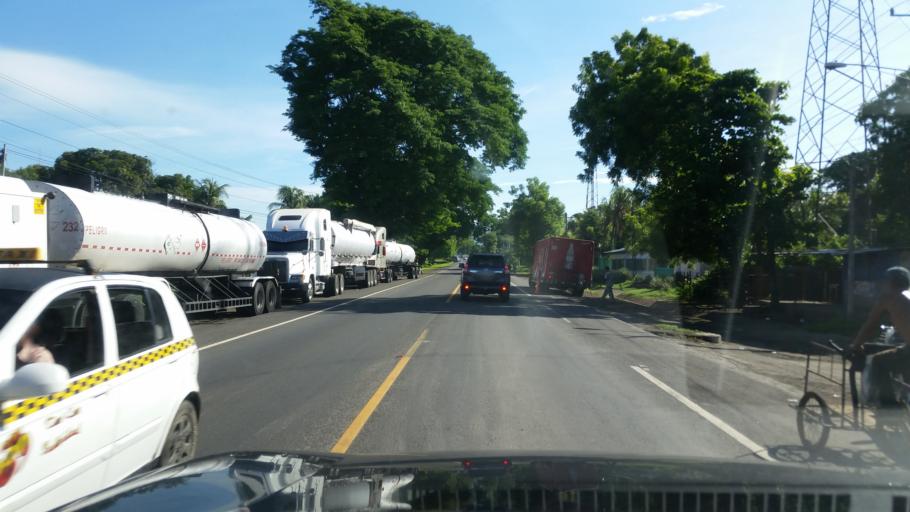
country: NI
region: Leon
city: Leon
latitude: 12.4631
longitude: -86.8666
